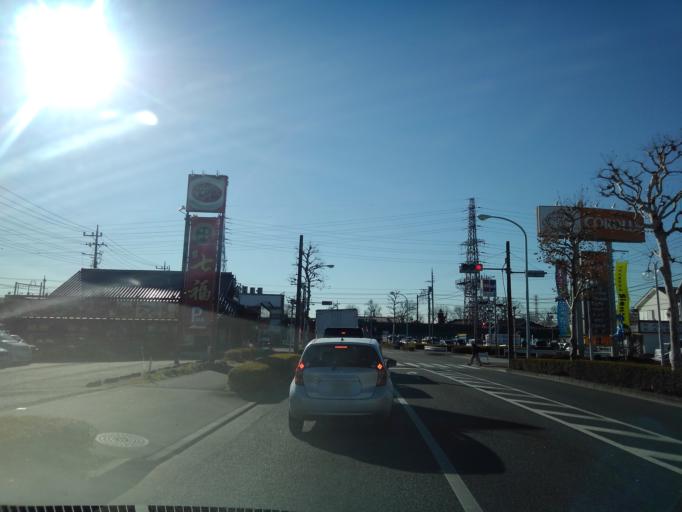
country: JP
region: Tokyo
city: Hino
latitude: 35.7291
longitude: 139.3824
